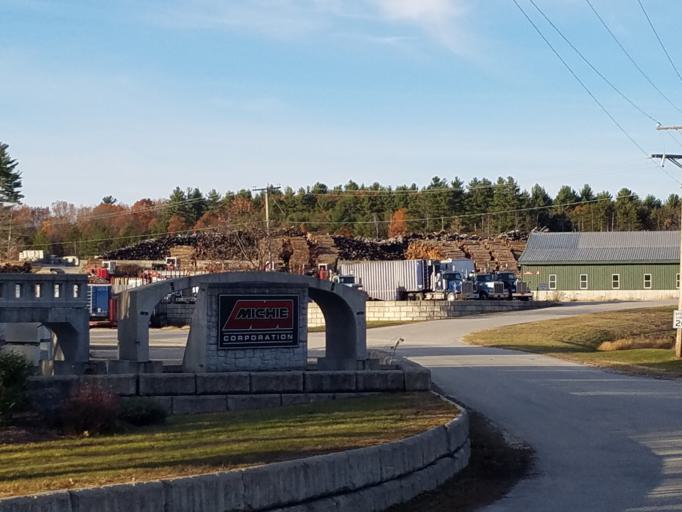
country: US
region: New Hampshire
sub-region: Merrimack County
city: Henniker
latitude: 43.1779
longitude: -71.7689
